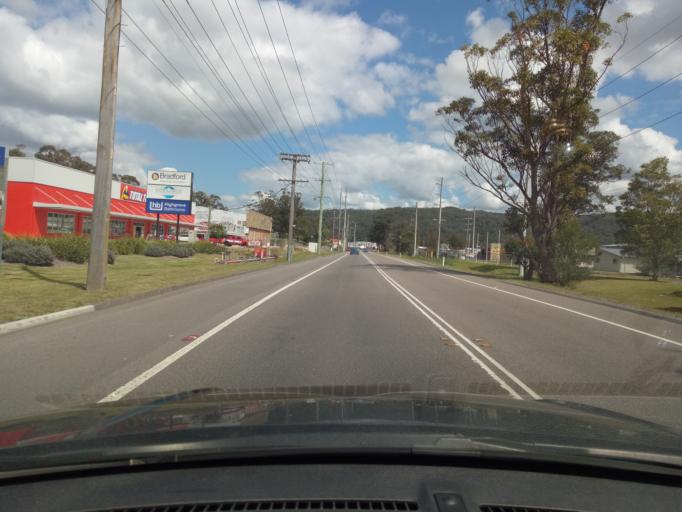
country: AU
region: New South Wales
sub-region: Gosford Shire
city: Gosford
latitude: -33.4154
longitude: 151.3311
